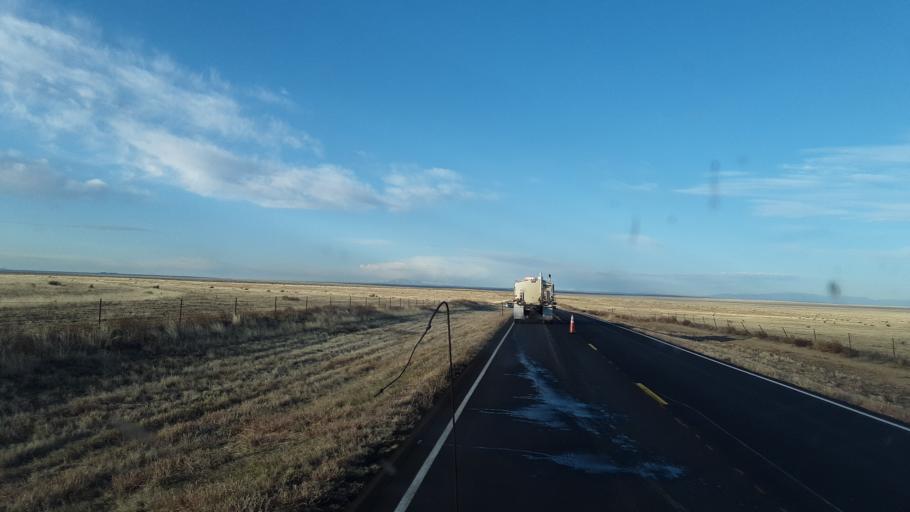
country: US
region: Colorado
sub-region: Otero County
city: Rocky Ford
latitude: 37.9636
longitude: -103.8398
